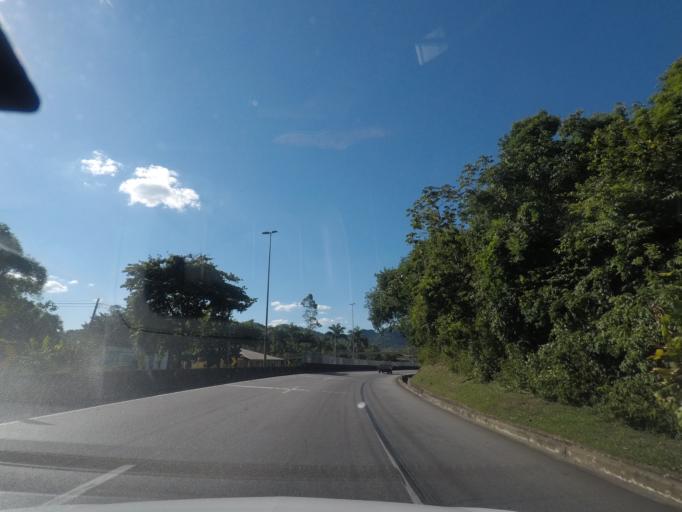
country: BR
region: Rio de Janeiro
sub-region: Petropolis
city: Petropolis
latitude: -22.6630
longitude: -43.1158
